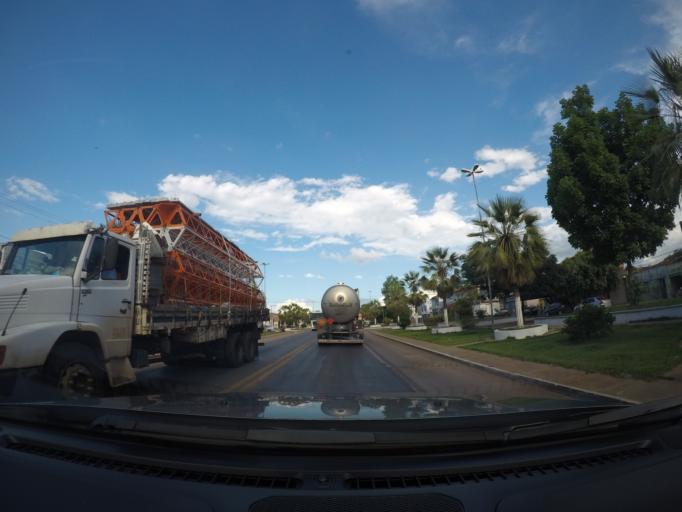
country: BR
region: Bahia
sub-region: Ibotirama
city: Ibotirama
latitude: -12.1784
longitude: -43.2201
